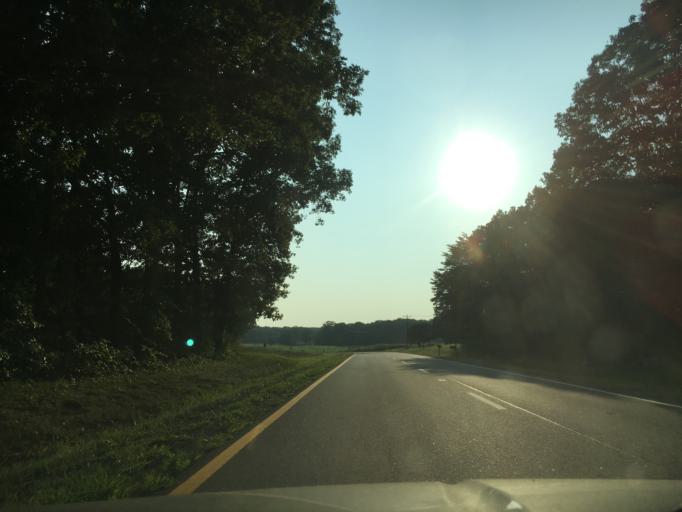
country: US
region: Virginia
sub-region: Prince Edward County
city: Hampden Sydney
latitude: 37.2944
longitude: -78.5974
